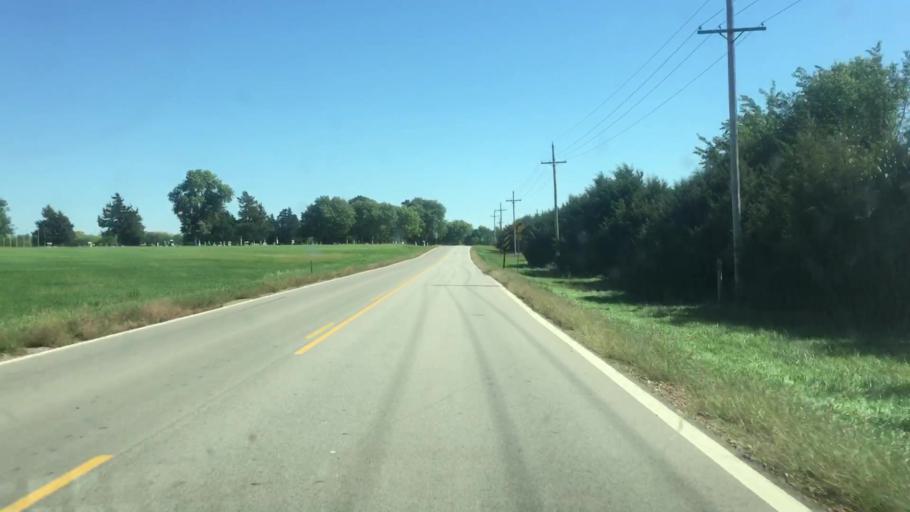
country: US
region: Kansas
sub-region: Jackson County
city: Holton
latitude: 39.6099
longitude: -95.7257
